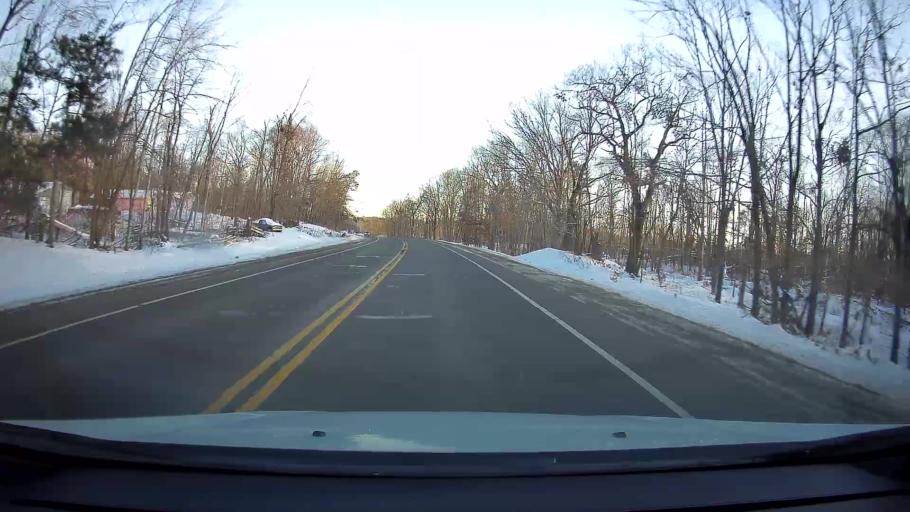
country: US
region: Wisconsin
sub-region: Barron County
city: Turtle Lake
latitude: 45.4140
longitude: -92.1335
